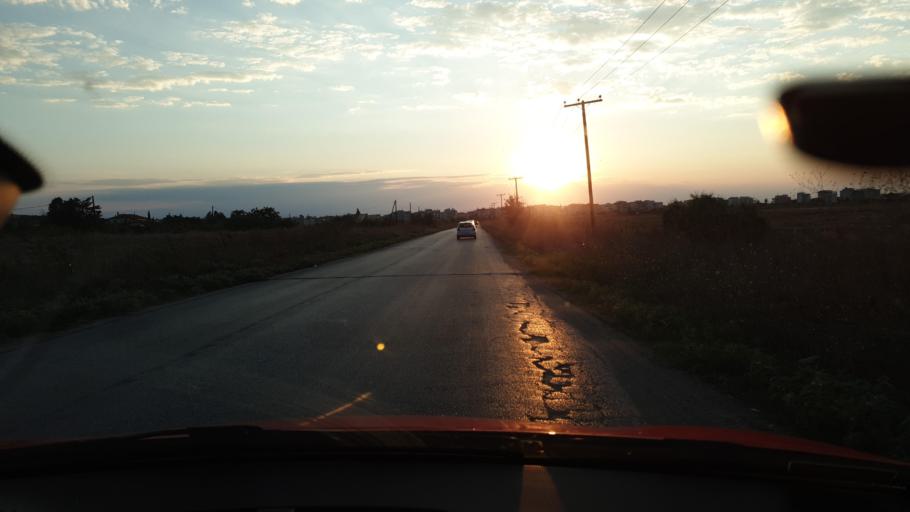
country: GR
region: Central Macedonia
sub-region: Nomos Thessalonikis
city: Peraia
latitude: 40.5082
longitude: 22.9469
